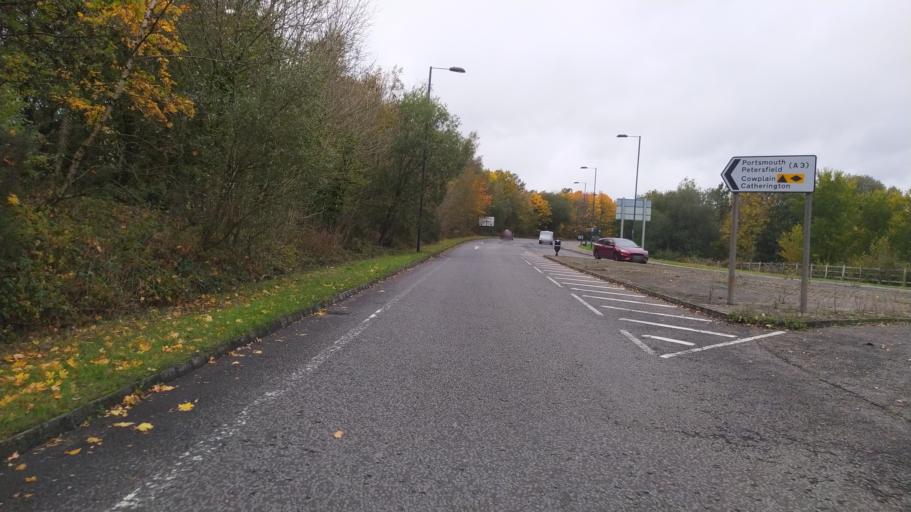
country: GB
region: England
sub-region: Hampshire
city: Cowplain
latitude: 50.9074
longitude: -1.0049
